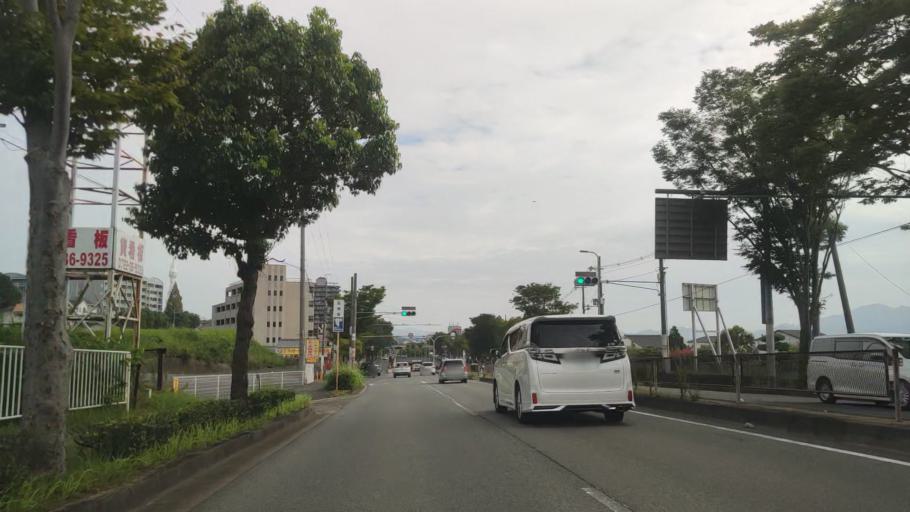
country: JP
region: Osaka
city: Tondabayashicho
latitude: 34.4886
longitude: 135.5825
